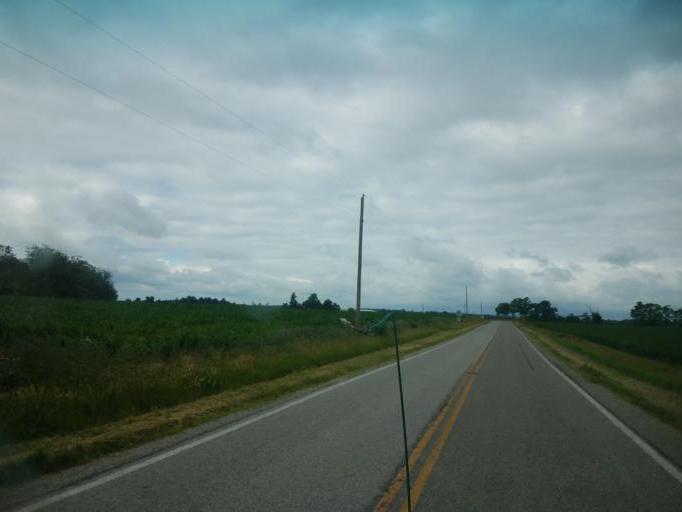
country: US
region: Ohio
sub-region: Champaign County
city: North Lewisburg
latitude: 40.4103
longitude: -83.5128
